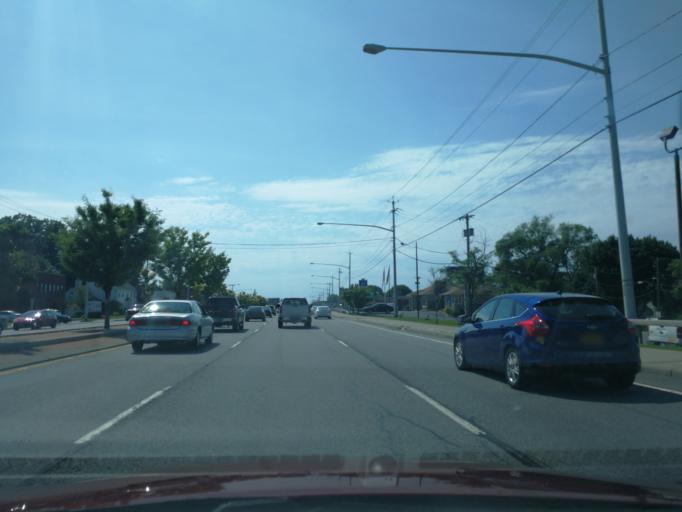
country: US
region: New York
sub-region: Monroe County
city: Greece
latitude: 43.2078
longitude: -77.6823
